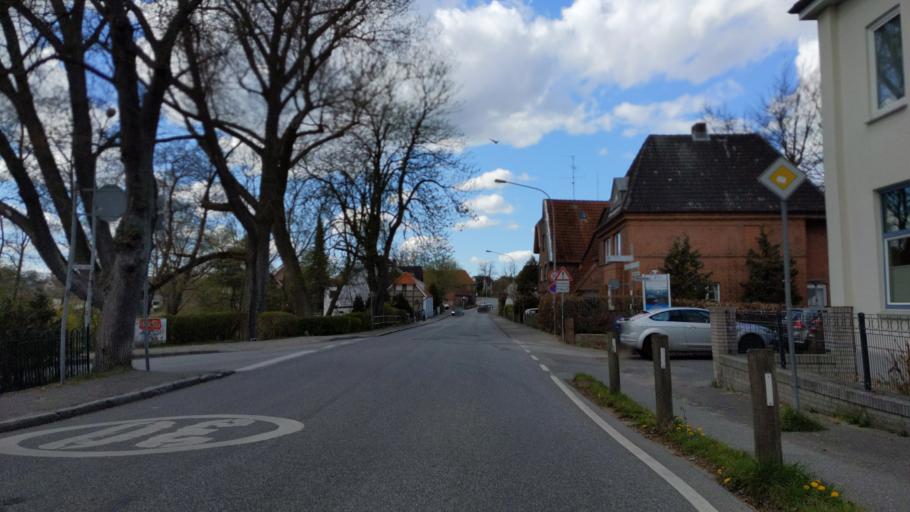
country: DE
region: Mecklenburg-Vorpommern
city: Selmsdorf
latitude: 53.8861
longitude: 10.8022
